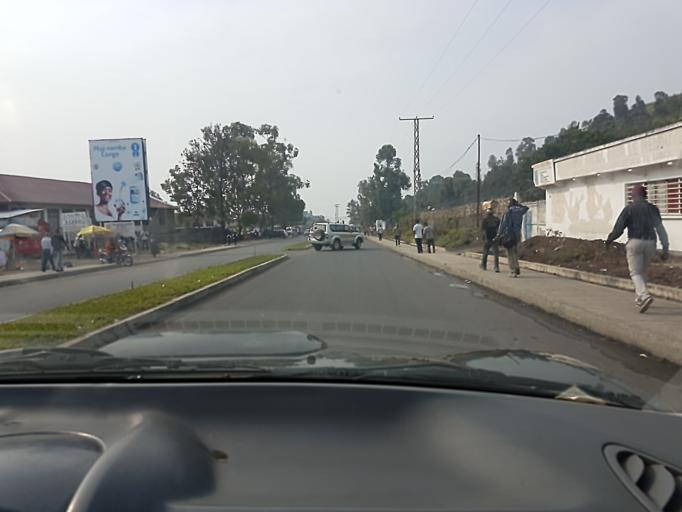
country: CD
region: Nord Kivu
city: Goma
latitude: -1.6806
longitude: 29.2285
